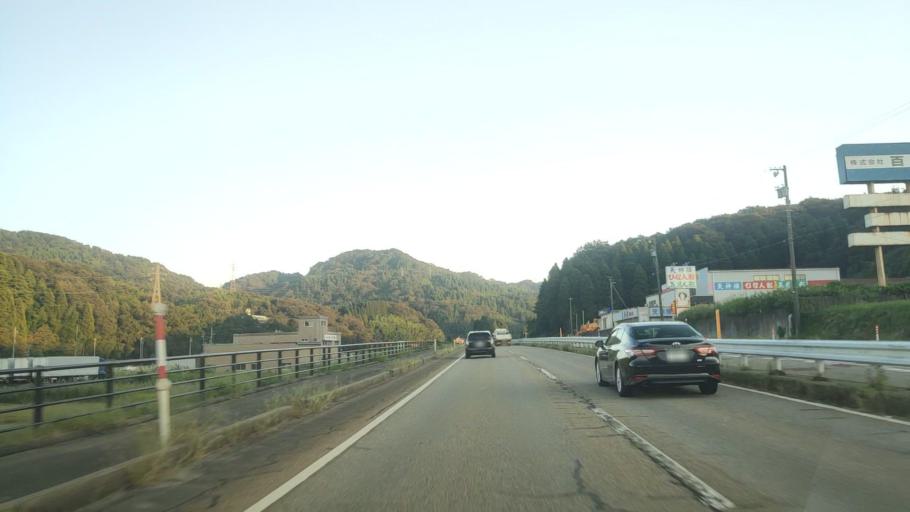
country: JP
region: Toyama
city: Himi
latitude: 36.8069
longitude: 136.9984
